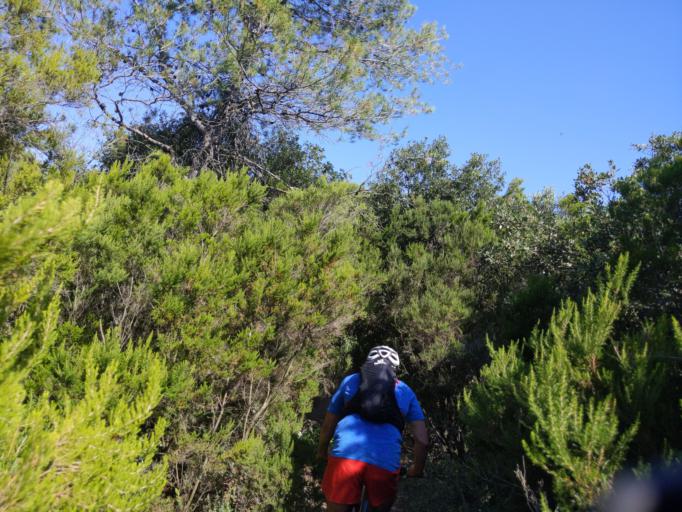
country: ES
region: Catalonia
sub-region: Provincia de Barcelona
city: Cerdanyola del Valles
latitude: 41.4647
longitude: 2.1340
